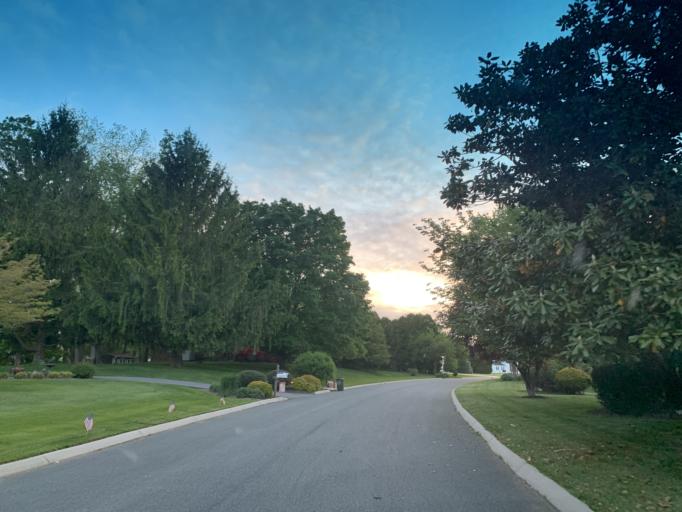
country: US
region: Maryland
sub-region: Harford County
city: South Bel Air
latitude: 39.5925
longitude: -76.2764
